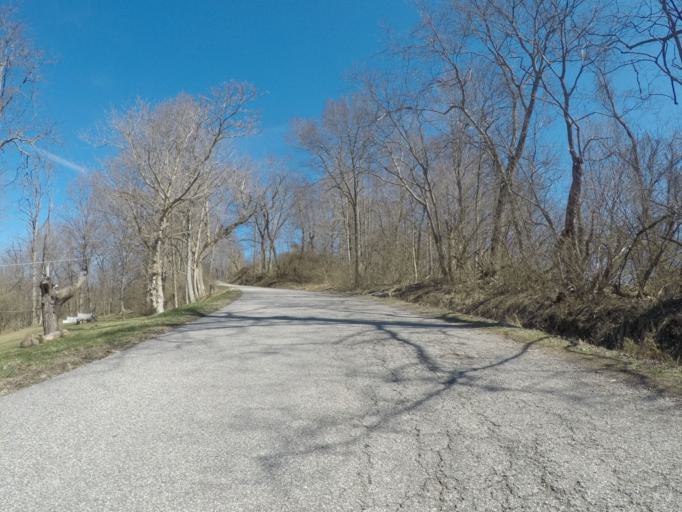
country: US
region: Ohio
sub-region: Lawrence County
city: Burlington
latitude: 38.4586
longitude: -82.4997
